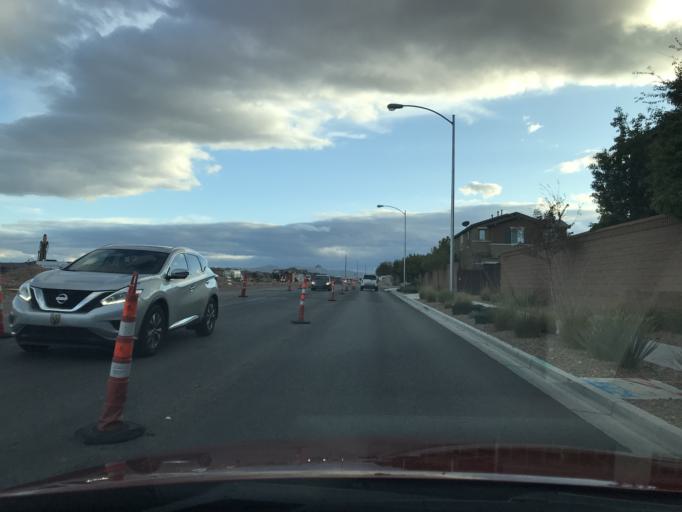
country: US
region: Nevada
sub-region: Clark County
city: Enterprise
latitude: 36.0325
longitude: -115.2790
